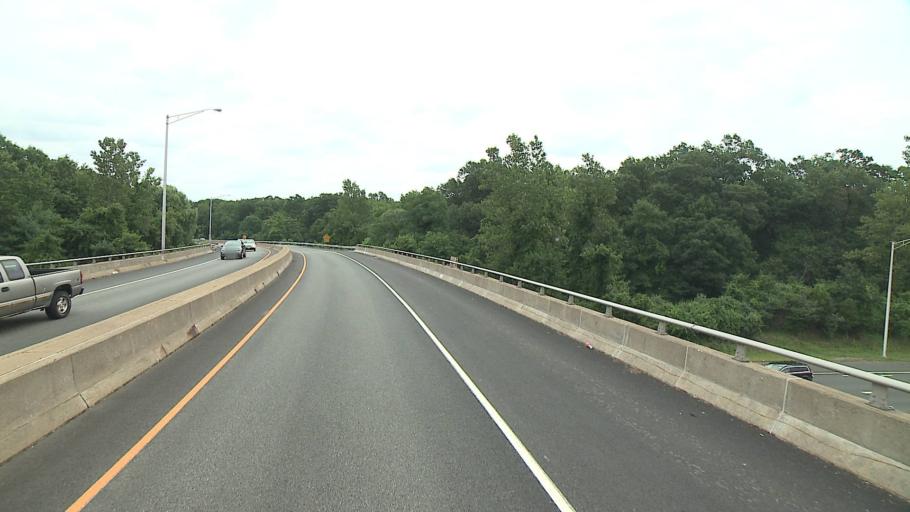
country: US
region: Connecticut
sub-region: Hartford County
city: Glastonbury
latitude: 41.7265
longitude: -72.6111
